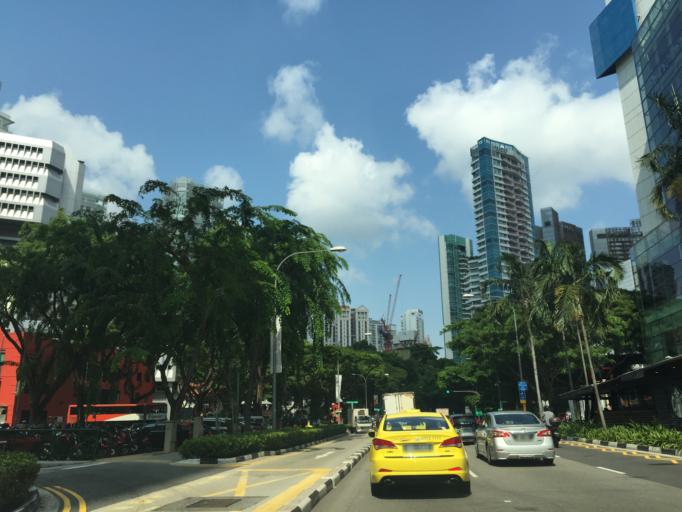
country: SG
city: Singapore
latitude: 1.3015
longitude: 103.8371
